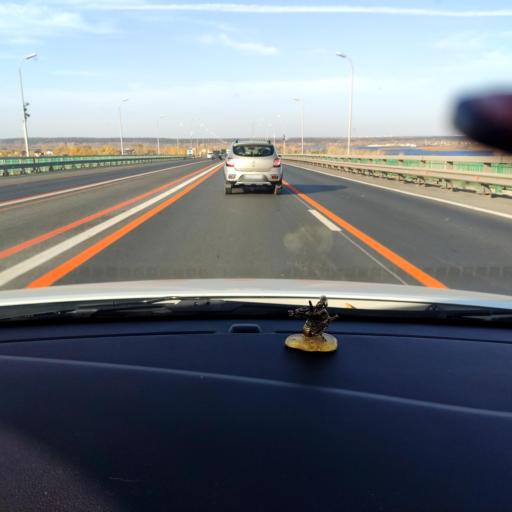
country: RU
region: Tatarstan
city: Osinovo
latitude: 55.7891
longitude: 48.8400
